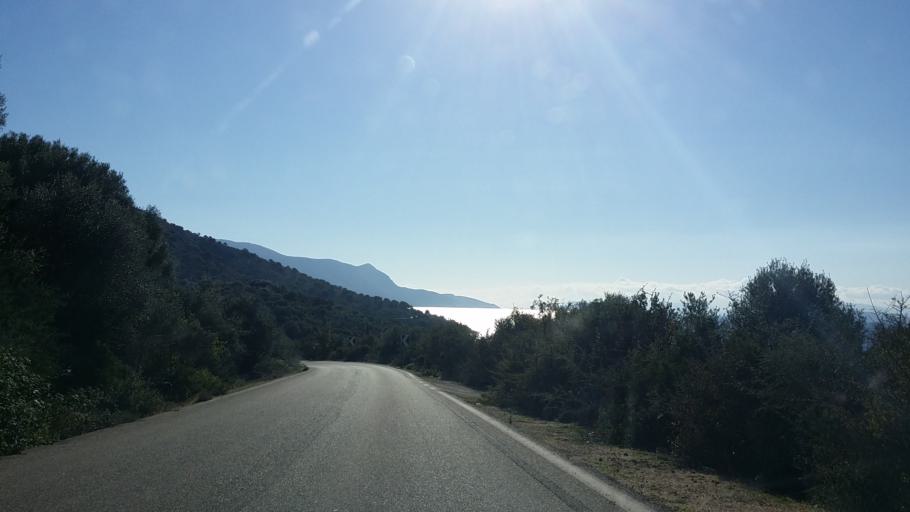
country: GR
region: West Greece
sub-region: Nomos Aitolias kai Akarnanias
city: Kandila
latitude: 38.7265
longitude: 20.8954
